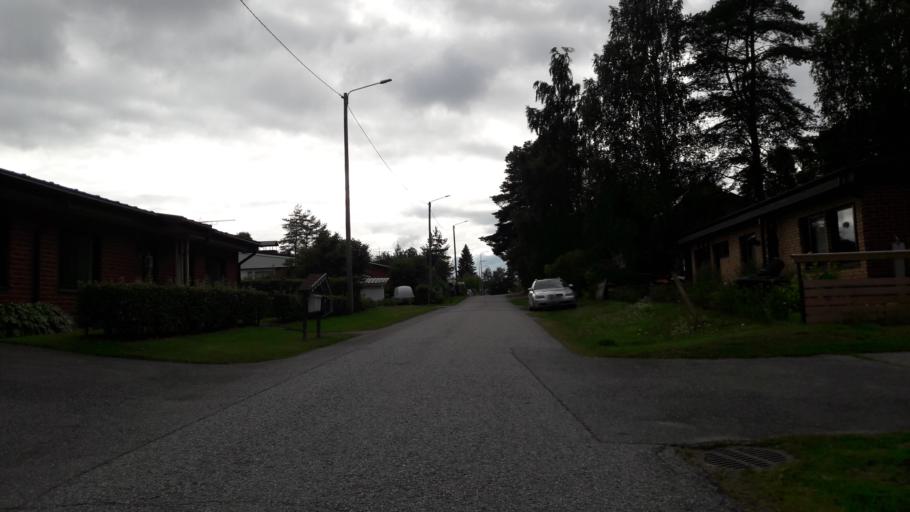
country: FI
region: North Karelia
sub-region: Joensuu
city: Joensuu
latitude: 62.5831
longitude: 29.8026
